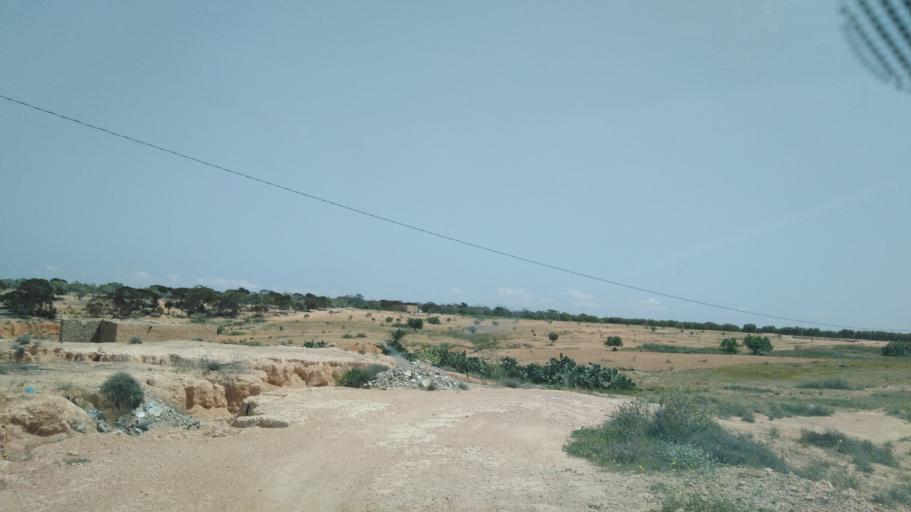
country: TN
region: Safaqis
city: Sfax
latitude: 34.7215
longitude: 10.5682
